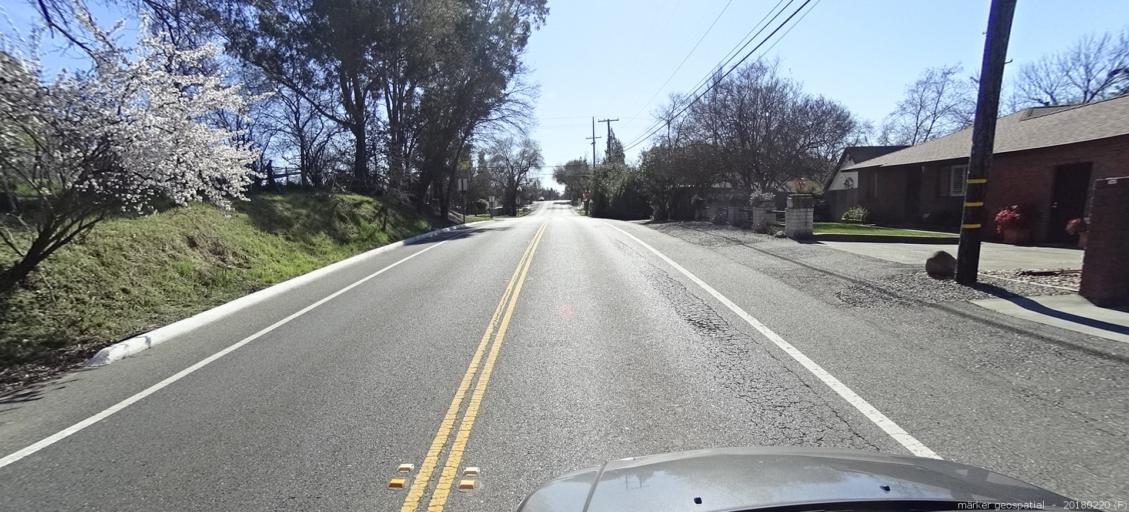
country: US
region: California
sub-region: Sacramento County
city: Orangevale
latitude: 38.6938
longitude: -121.2348
